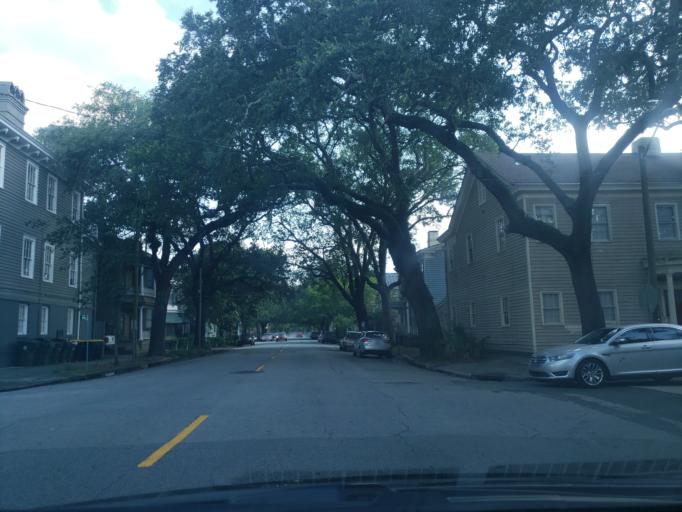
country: US
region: Georgia
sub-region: Chatham County
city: Savannah
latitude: 32.0656
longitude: -81.0994
